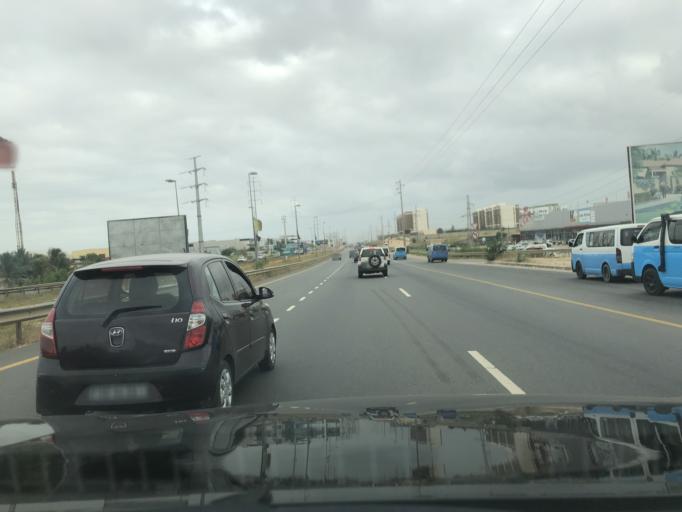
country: AO
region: Luanda
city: Luanda
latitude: -8.9739
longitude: 13.2230
